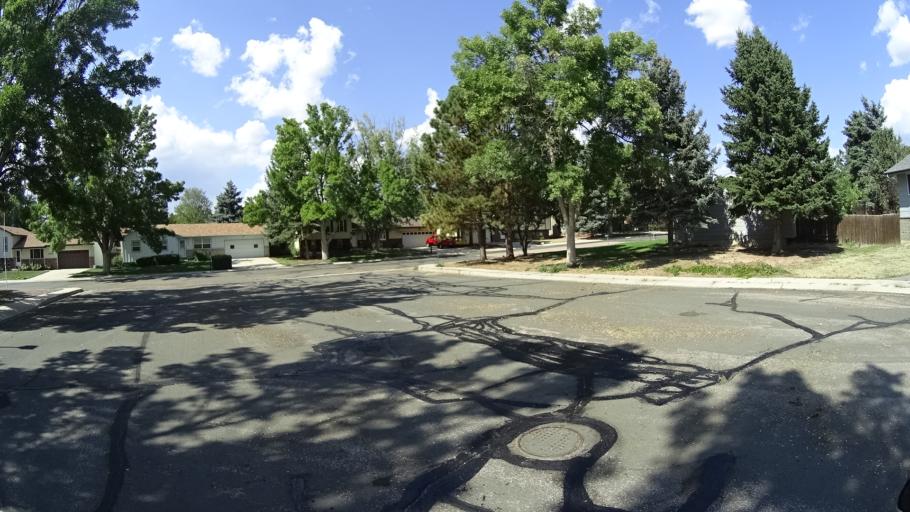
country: US
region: Colorado
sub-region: El Paso County
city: Cimarron Hills
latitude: 38.8752
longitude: -104.7493
